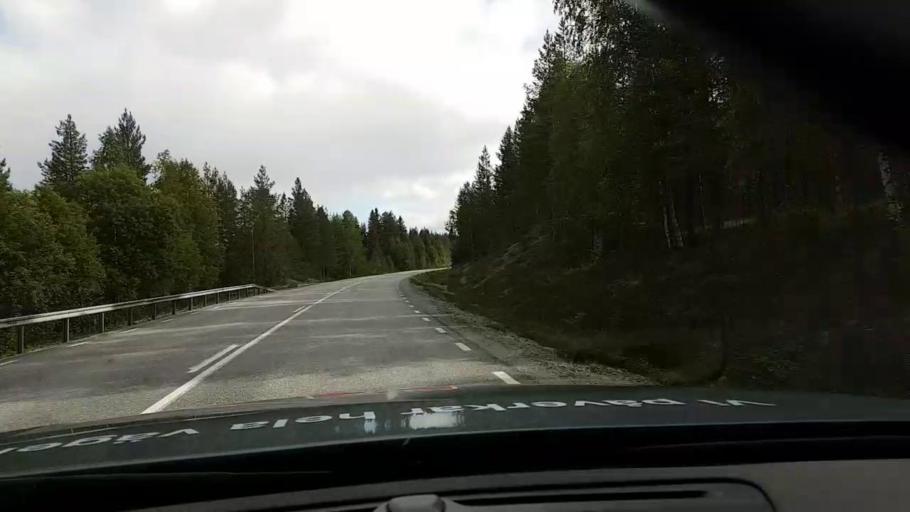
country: SE
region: Vaesternorrland
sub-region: OErnskoeldsviks Kommun
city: Bredbyn
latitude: 63.6342
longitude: 17.9076
